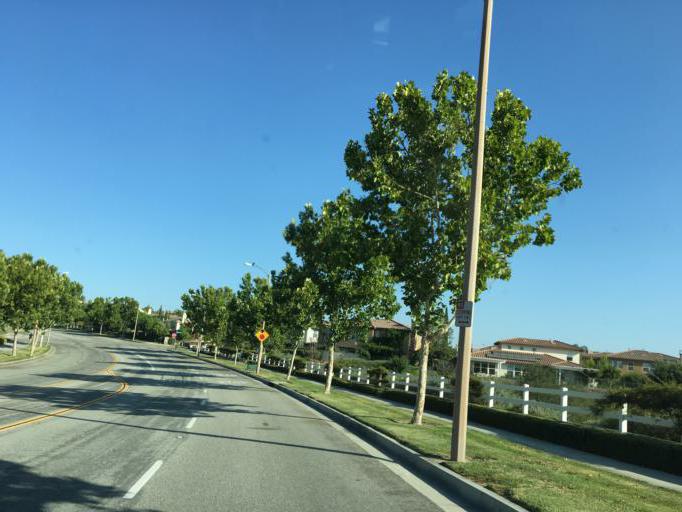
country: US
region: California
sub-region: Los Angeles County
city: Valencia
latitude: 34.4061
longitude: -118.5899
